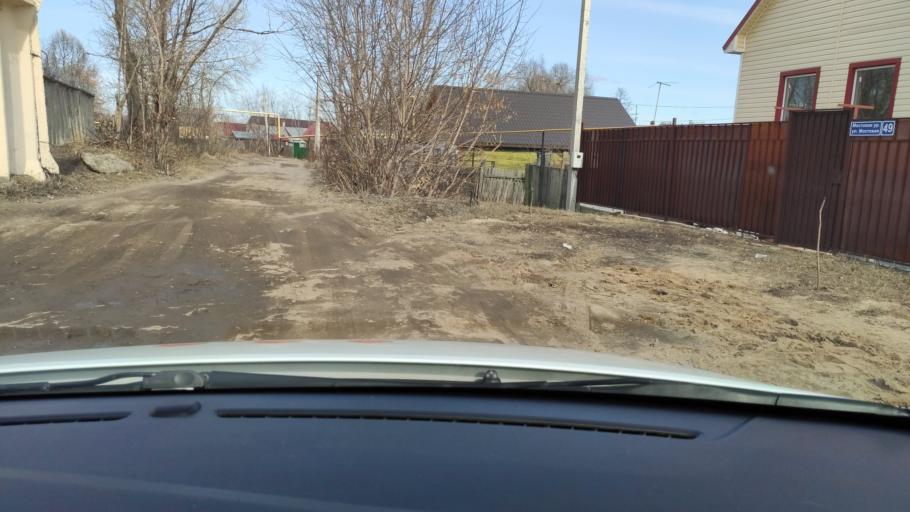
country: RU
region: Tatarstan
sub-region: Gorod Kazan'
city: Kazan
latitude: 55.7497
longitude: 49.1384
